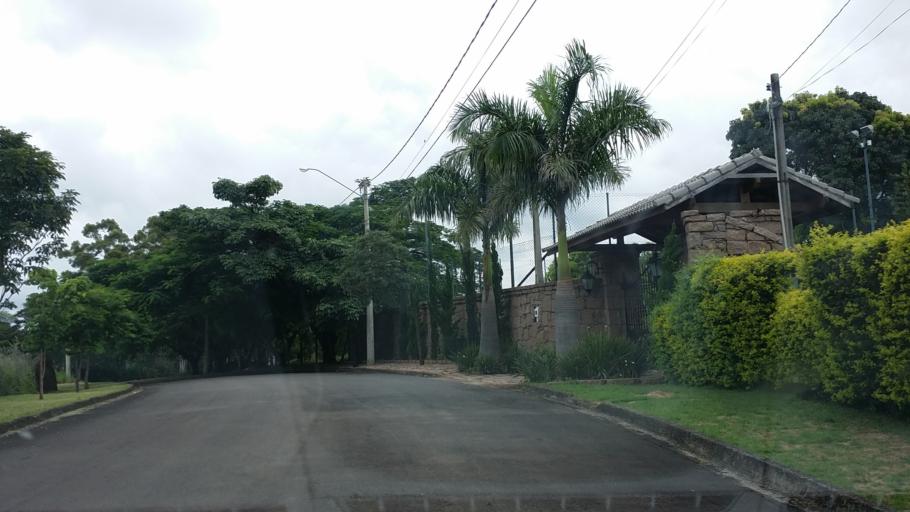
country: BR
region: Sao Paulo
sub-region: Indaiatuba
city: Indaiatuba
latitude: -23.1430
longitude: -47.1841
